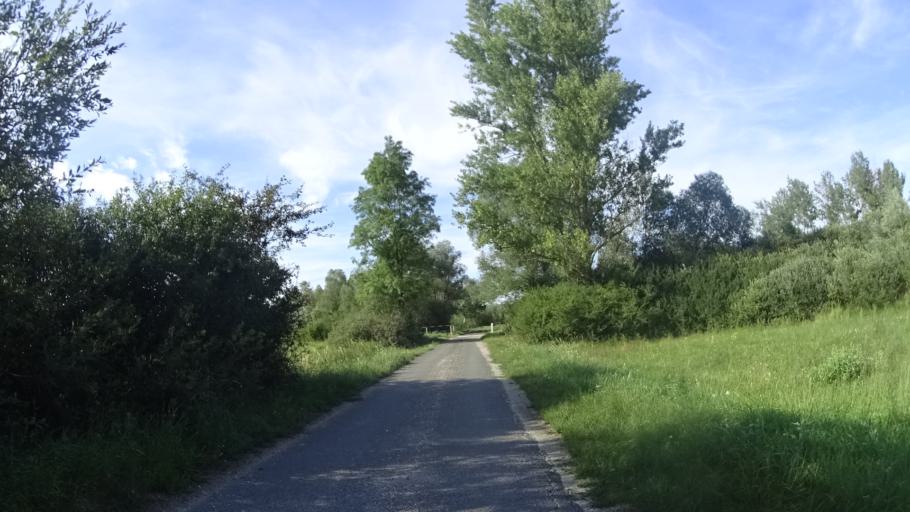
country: AT
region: Lower Austria
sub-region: Politischer Bezirk Ganserndorf
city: Drosing
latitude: 48.5609
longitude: 16.9579
